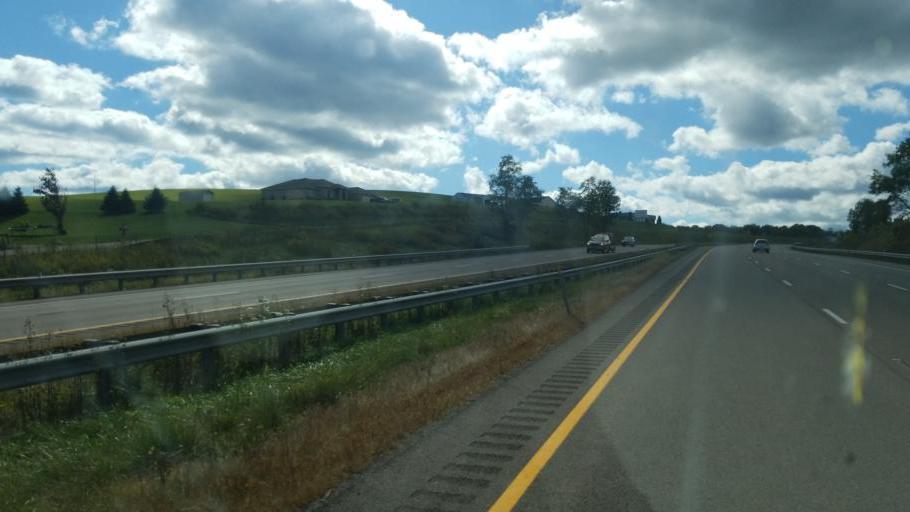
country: US
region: Pennsylvania
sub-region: Somerset County
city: Meyersdale
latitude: 39.6932
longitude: -79.1461
